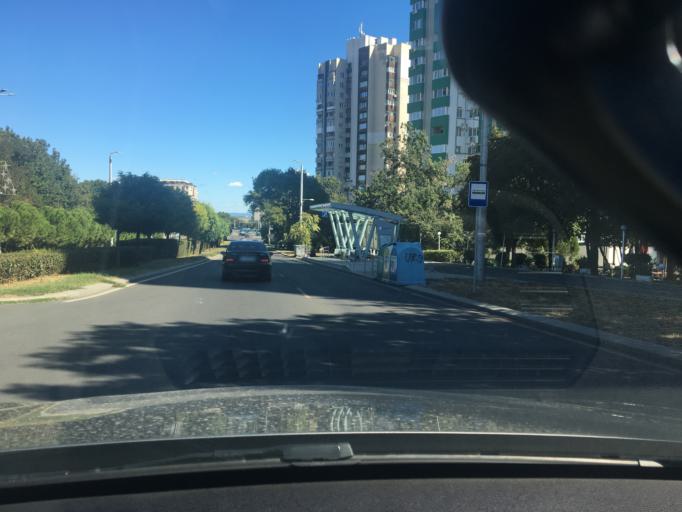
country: BG
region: Burgas
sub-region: Obshtina Burgas
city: Burgas
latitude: 42.5192
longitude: 27.4633
